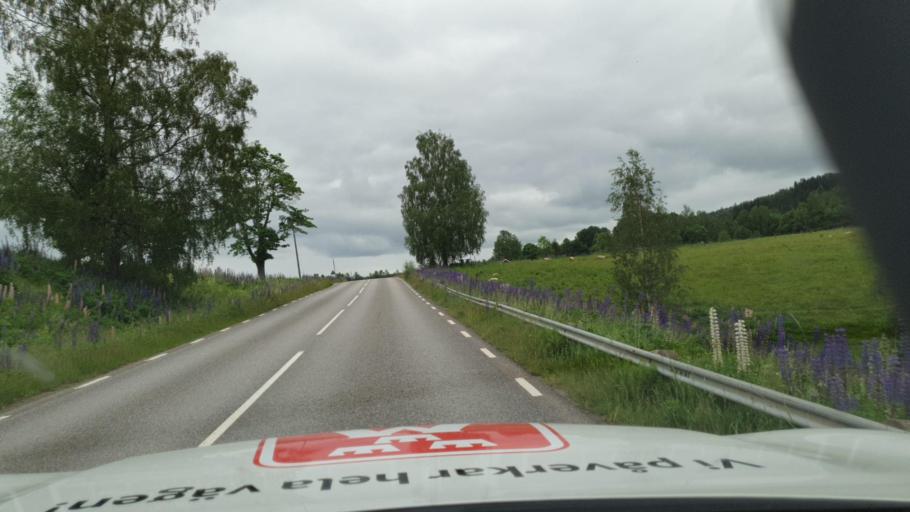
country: SE
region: Vaermland
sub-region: Sunne Kommun
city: Sunne
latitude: 59.8122
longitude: 13.0269
